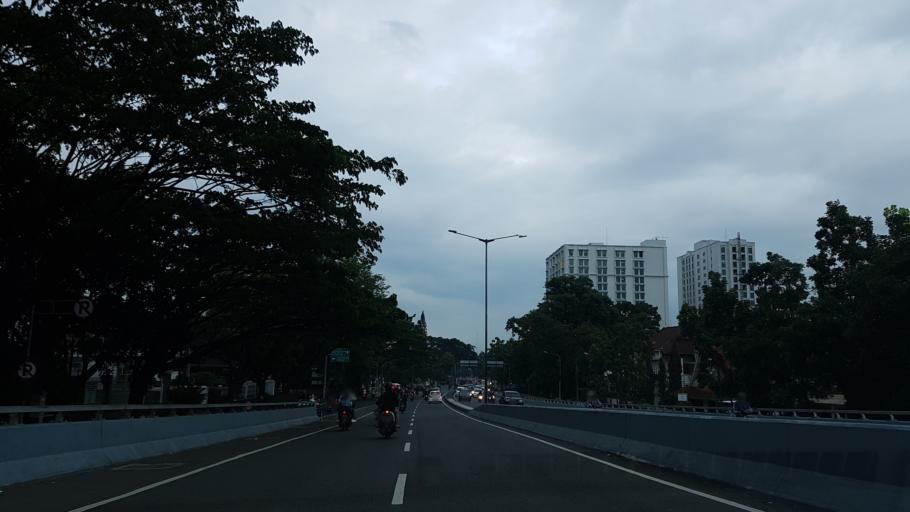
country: ID
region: West Java
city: Bandung
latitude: -6.8989
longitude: 107.6144
